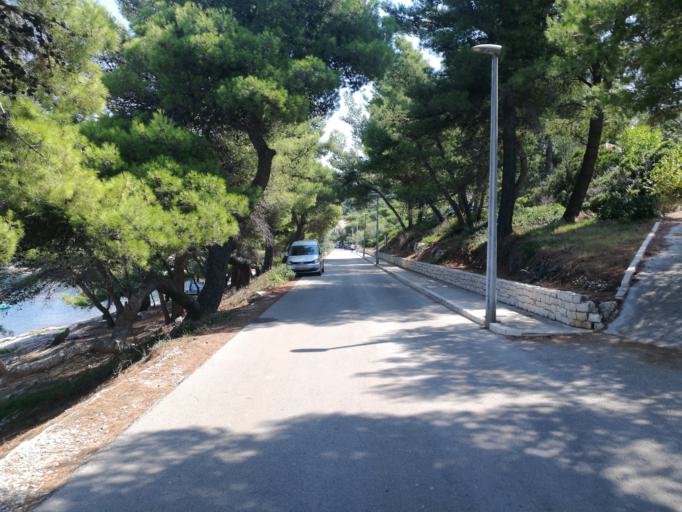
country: HR
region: Splitsko-Dalmatinska
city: Postira
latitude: 43.3764
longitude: 16.6375
